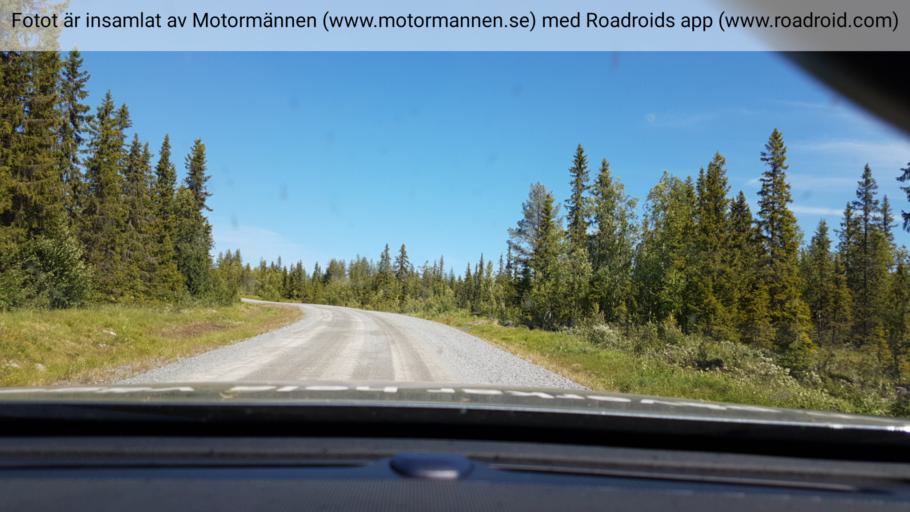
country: SE
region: Vaesterbotten
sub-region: Vilhelmina Kommun
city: Sjoberg
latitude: 64.7186
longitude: 15.7808
